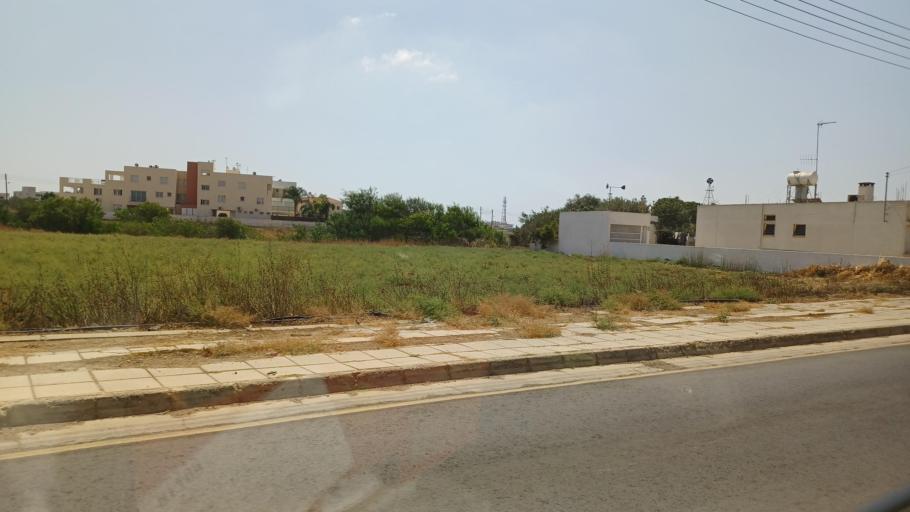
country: CY
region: Ammochostos
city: Deryneia
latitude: 35.0576
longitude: 33.9631
